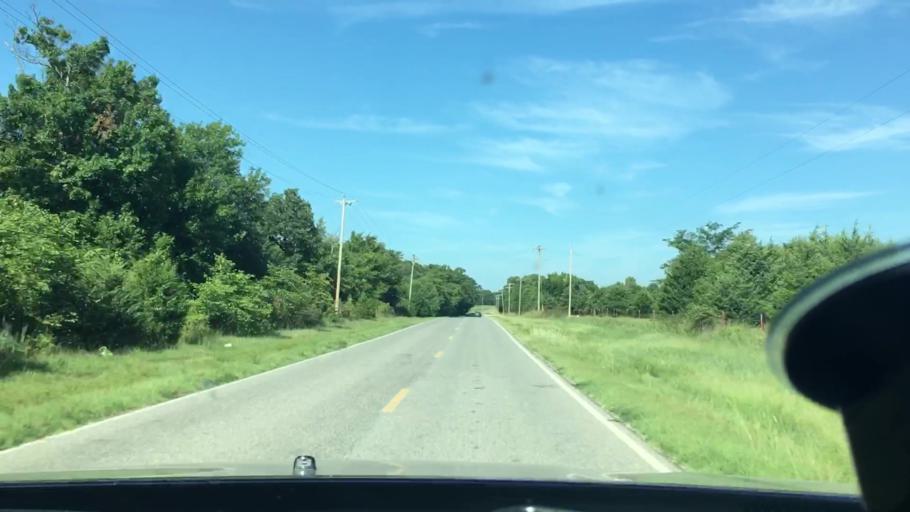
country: US
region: Oklahoma
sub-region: Johnston County
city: Tishomingo
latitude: 34.2734
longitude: -96.4447
